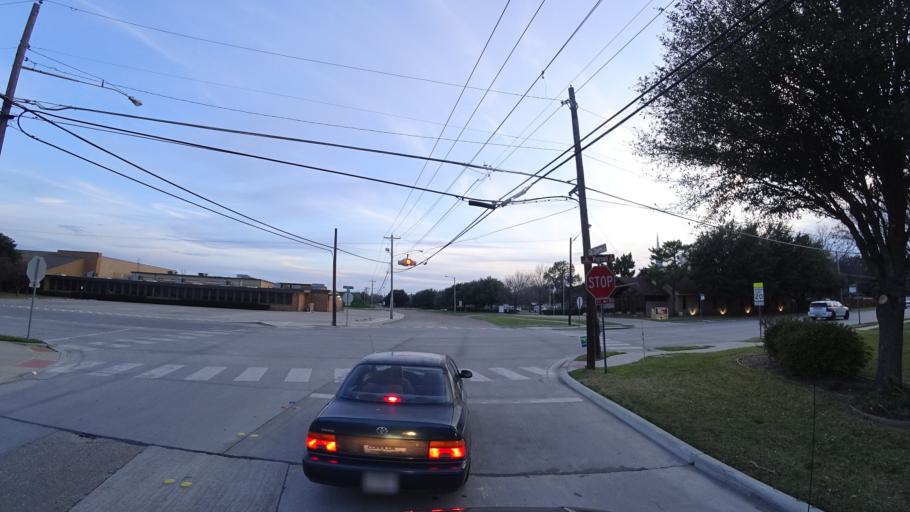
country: US
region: Texas
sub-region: Denton County
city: Lewisville
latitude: 33.0421
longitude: -96.9966
